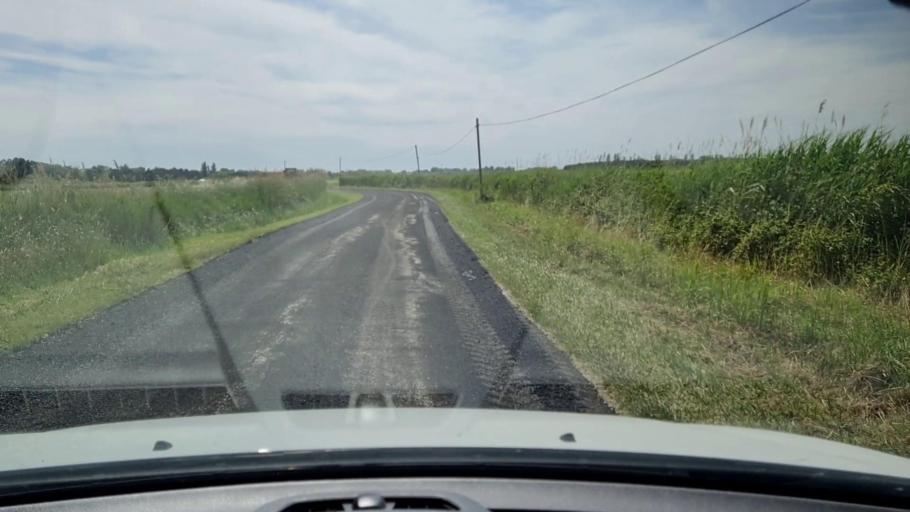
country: FR
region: Provence-Alpes-Cote d'Azur
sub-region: Departement des Bouches-du-Rhone
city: Saintes-Maries-de-la-Mer
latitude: 43.5554
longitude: 4.3779
